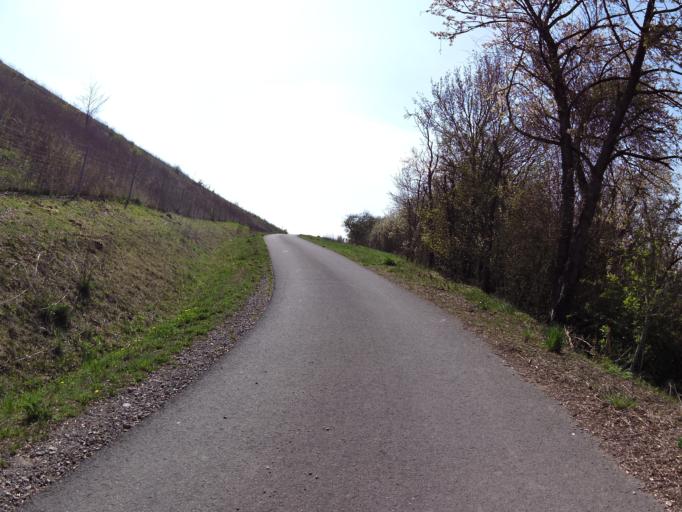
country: DE
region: Bavaria
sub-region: Regierungsbezirk Unterfranken
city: Theilheim
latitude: 49.7545
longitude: 10.0460
